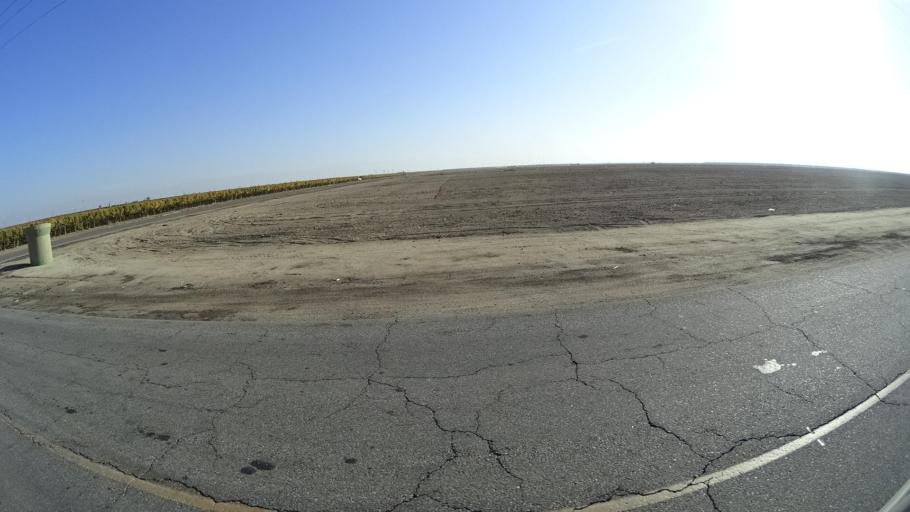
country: US
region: California
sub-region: Tulare County
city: Richgrove
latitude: 35.7686
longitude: -119.1697
